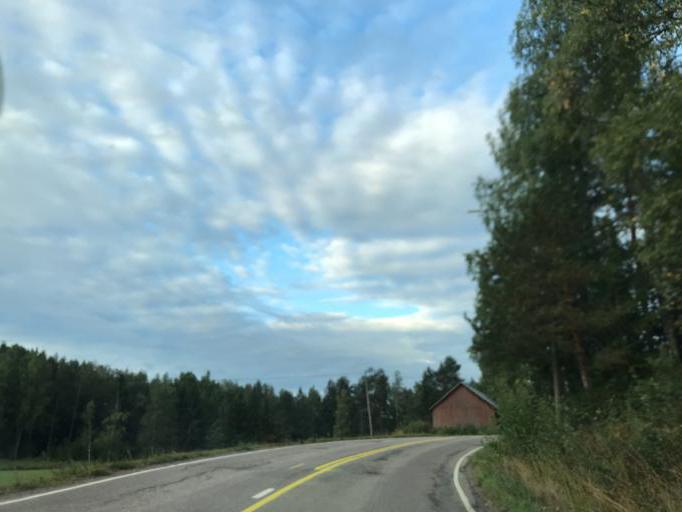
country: FI
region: Uusimaa
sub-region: Helsinki
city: Vihti
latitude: 60.3813
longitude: 24.5245
